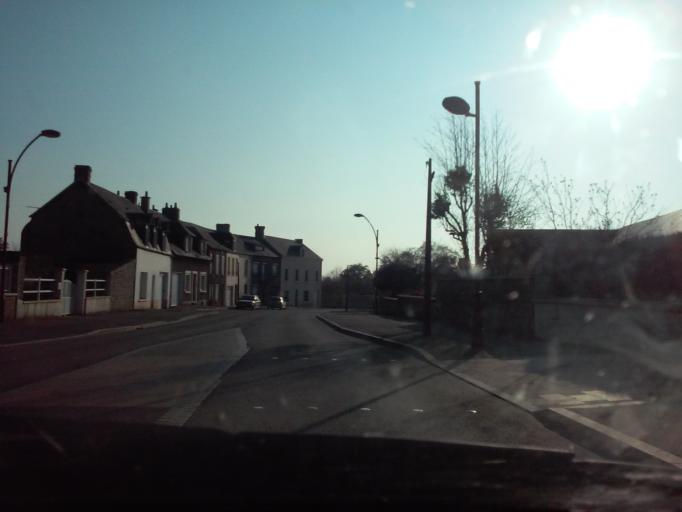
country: FR
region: Lower Normandy
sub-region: Departement du Calvados
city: Villers-Bocage
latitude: 49.0816
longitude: -0.6491
